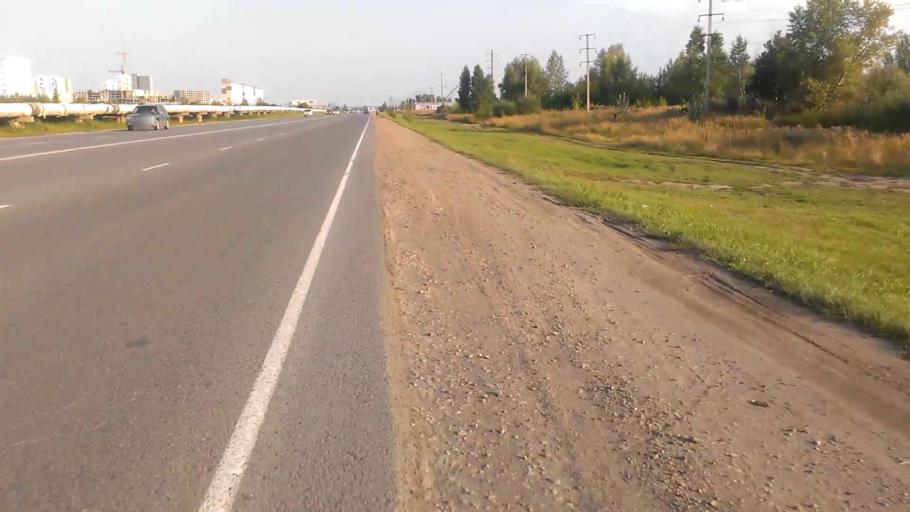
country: RU
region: Altai Krai
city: Novosilikatnyy
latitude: 53.3459
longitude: 83.6330
